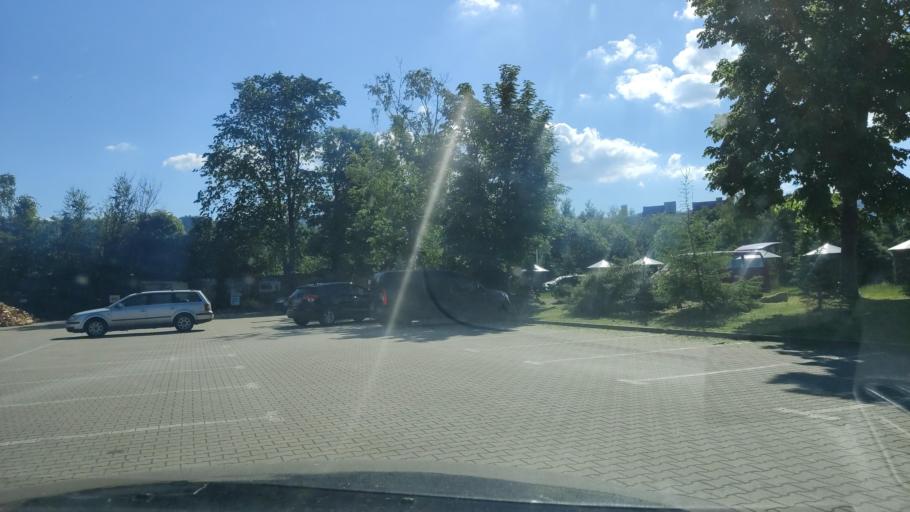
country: PL
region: Lower Silesian Voivodeship
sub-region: Powiat jeleniogorski
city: Kowary
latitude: 50.7980
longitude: 15.8342
